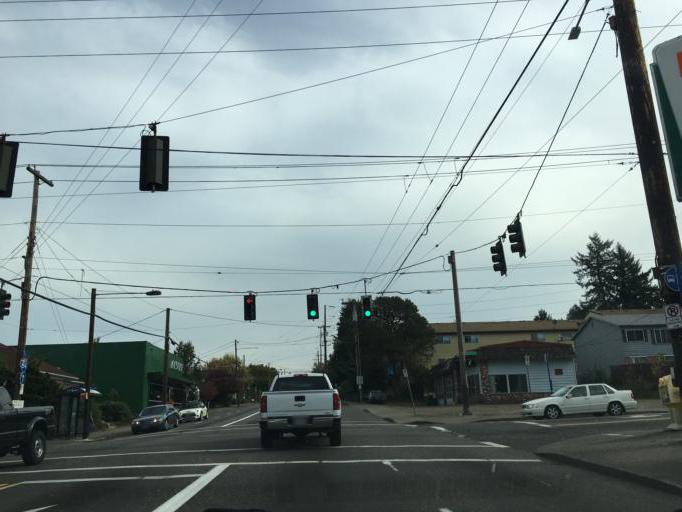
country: US
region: Oregon
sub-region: Multnomah County
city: Lents
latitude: 45.5228
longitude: -122.6026
